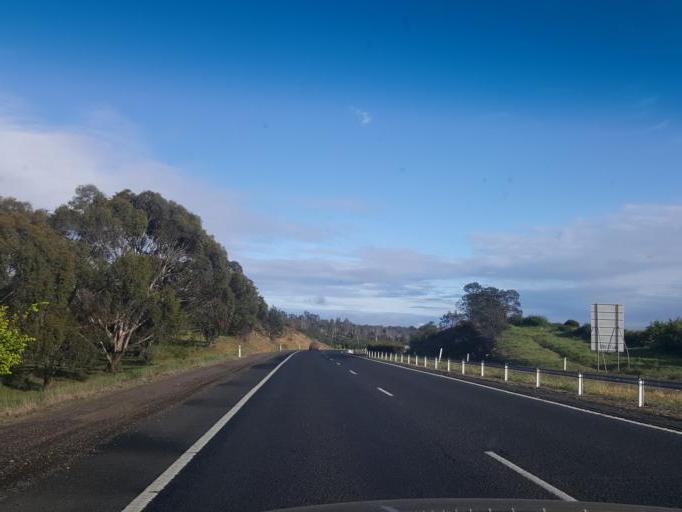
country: AU
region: Tasmania
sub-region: Northern Midlands
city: Perth
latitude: -41.5244
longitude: 147.1816
